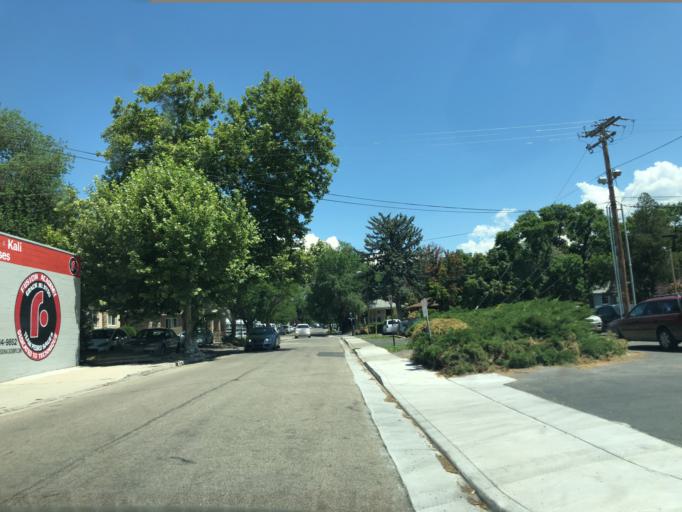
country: US
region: Utah
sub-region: Salt Lake County
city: South Salt Lake
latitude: 40.7221
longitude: -111.8736
